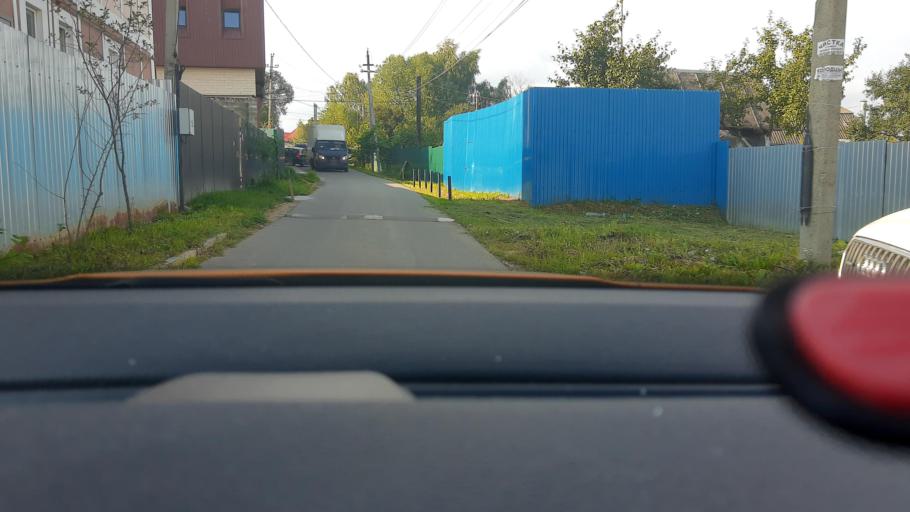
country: RU
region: Moskovskaya
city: Skhodnya
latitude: 55.9904
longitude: 37.3289
